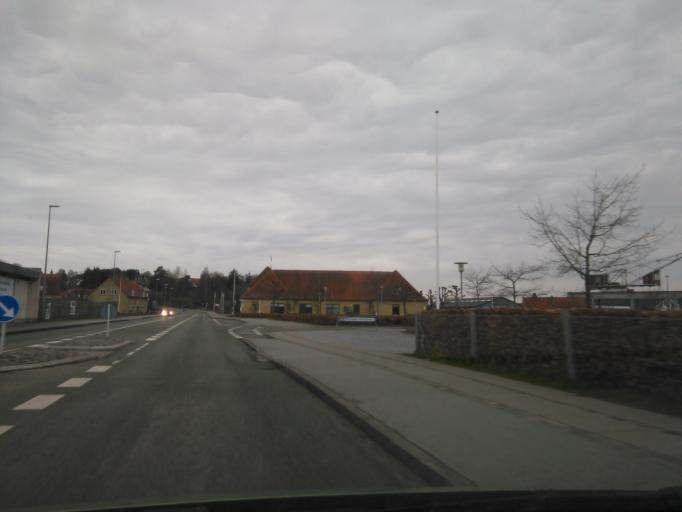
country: DK
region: North Denmark
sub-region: Mariagerfjord Kommune
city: Mariager
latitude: 56.6527
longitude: 9.9813
